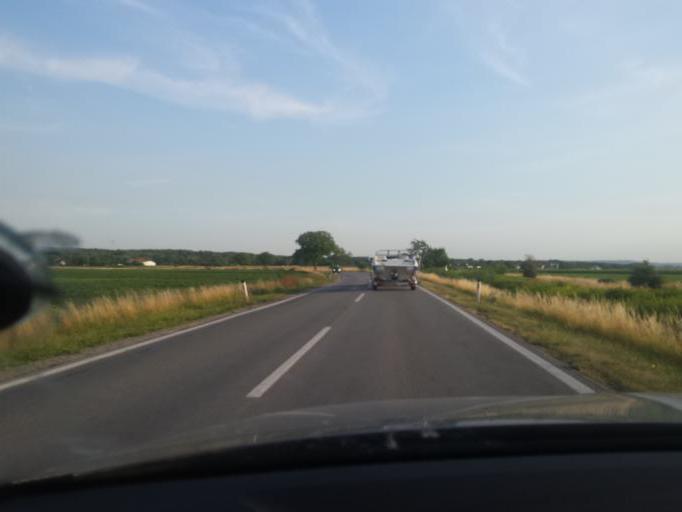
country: AT
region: Lower Austria
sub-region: Politischer Bezirk Bruck an der Leitha
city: Rohrau
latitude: 48.0764
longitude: 16.8611
